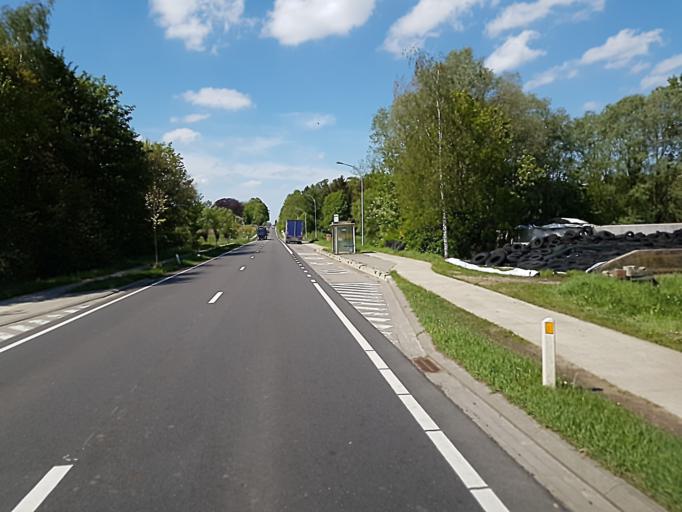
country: BE
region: Flanders
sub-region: Provincie Vlaams-Brabant
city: Glabbeek-Zuurbemde
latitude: 50.8476
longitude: 4.9078
